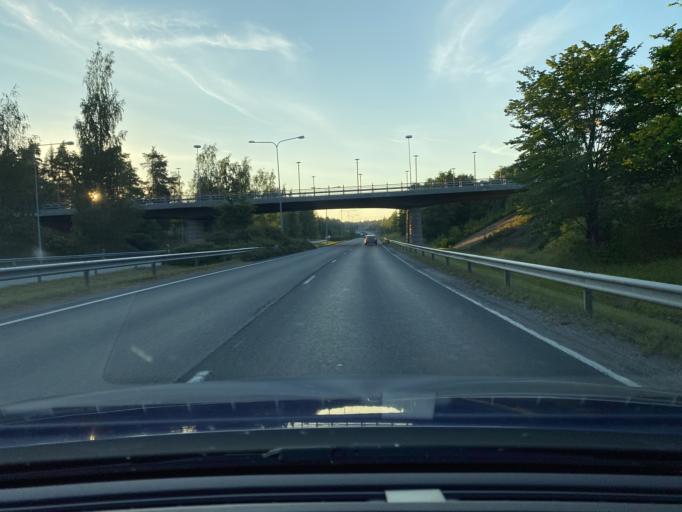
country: FI
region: Pirkanmaa
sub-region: Tampere
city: Pirkkala
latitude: 61.5196
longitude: 23.6493
